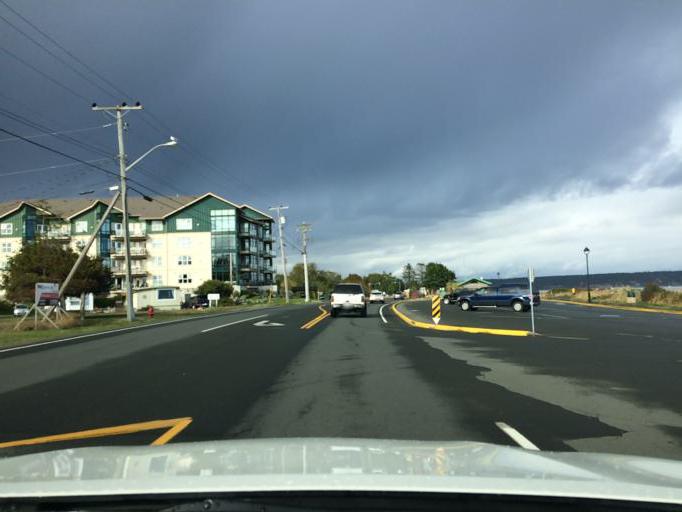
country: CA
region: British Columbia
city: Campbell River
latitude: 49.9636
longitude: -125.2094
